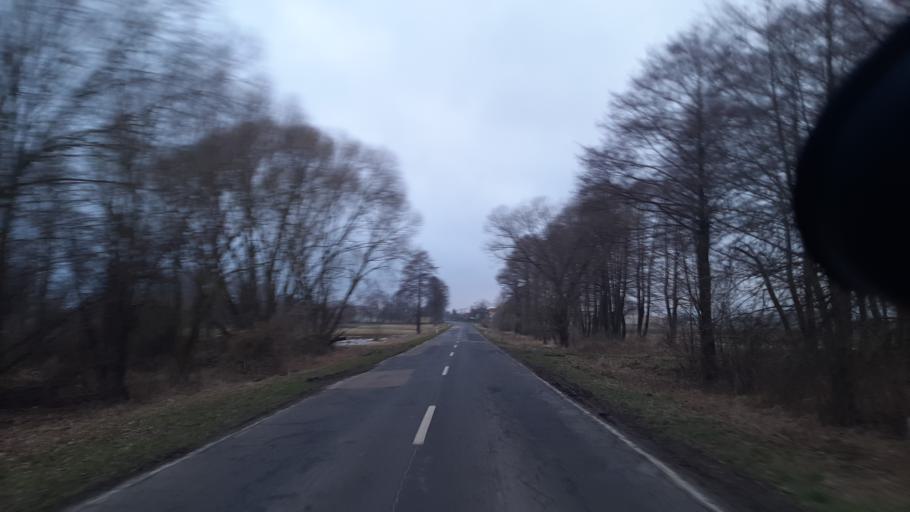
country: PL
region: Lublin Voivodeship
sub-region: Powiat parczewski
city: Debowa Kloda
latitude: 51.6187
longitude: 23.0985
